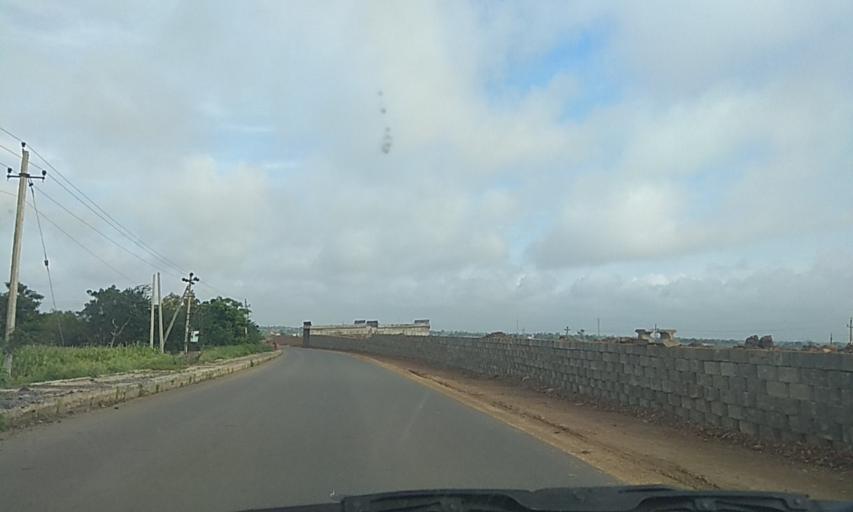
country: IN
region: Karnataka
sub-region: Haveri
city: Haveri
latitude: 14.8531
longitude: 75.3291
